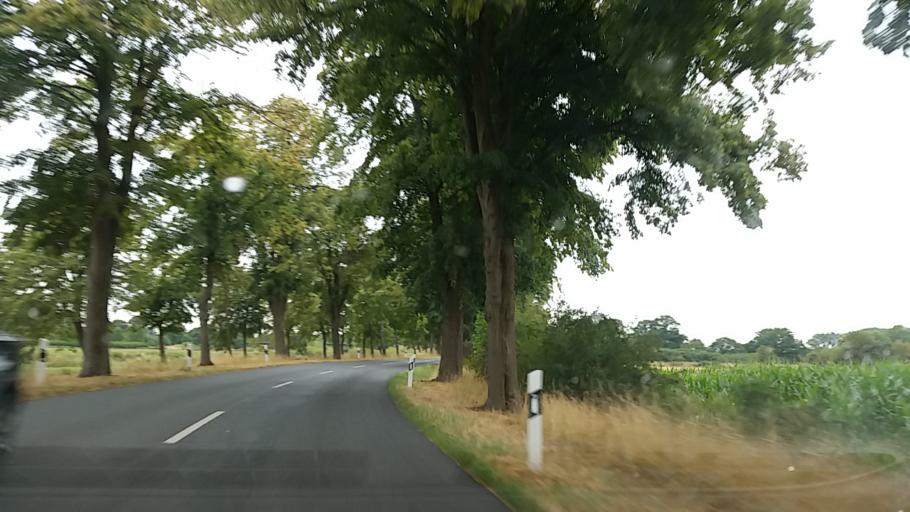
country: DE
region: Lower Saxony
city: Gilten
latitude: 52.6998
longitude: 9.5979
